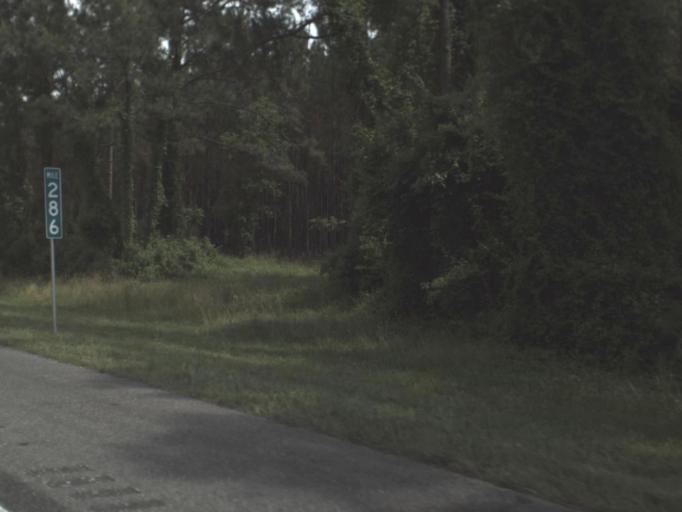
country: US
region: Florida
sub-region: Suwannee County
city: Live Oak
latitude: 30.3048
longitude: -82.9192
